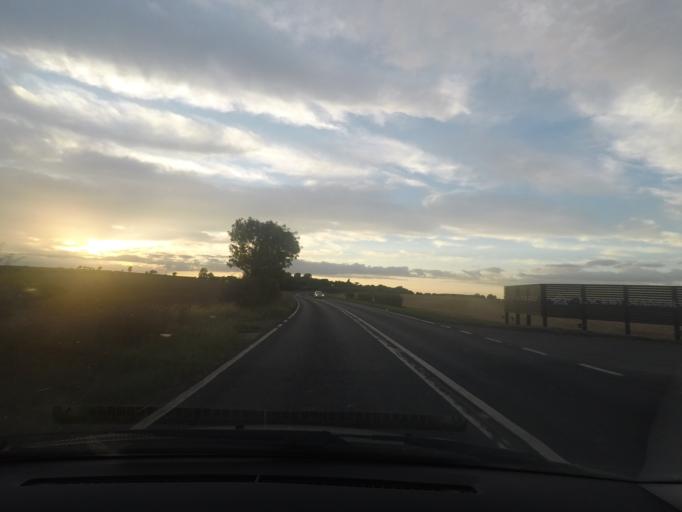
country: GB
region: England
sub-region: North East Lincolnshire
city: Laceby
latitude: 53.5254
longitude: -0.1653
